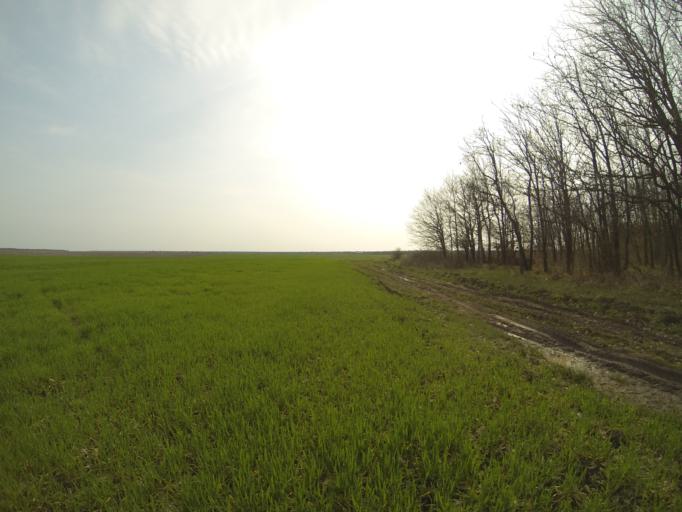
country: RO
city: Varvoru
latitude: 44.2718
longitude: 23.6669
